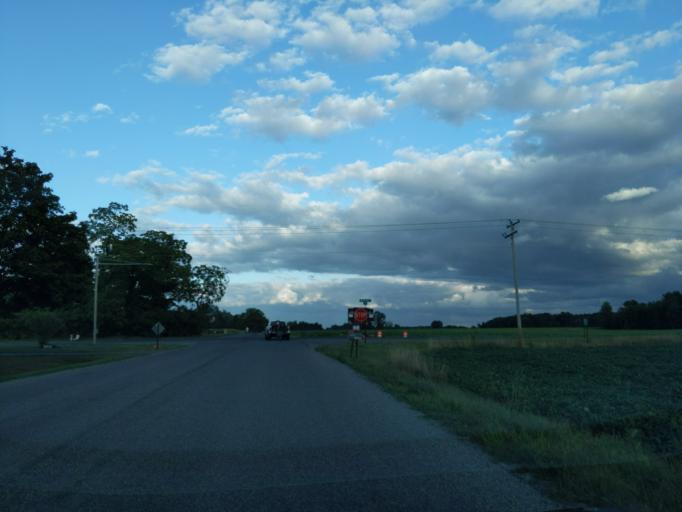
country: US
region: Michigan
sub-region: Ingham County
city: Holt
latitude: 42.5968
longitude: -84.5632
